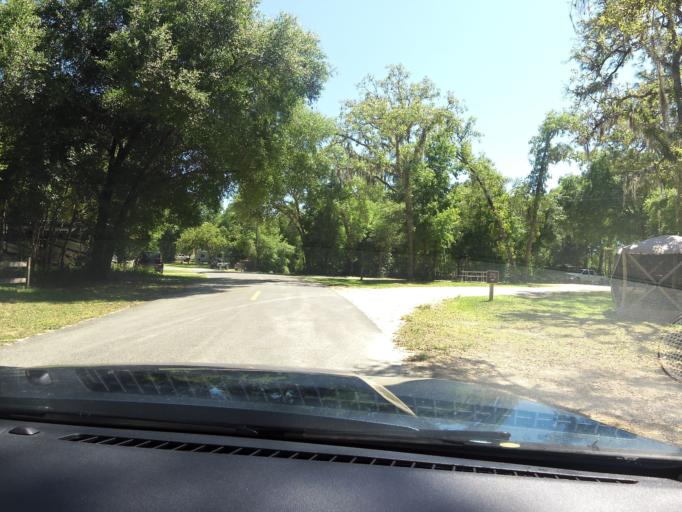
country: US
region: Florida
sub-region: Clay County
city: Keystone Heights
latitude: 29.8212
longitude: -81.9461
